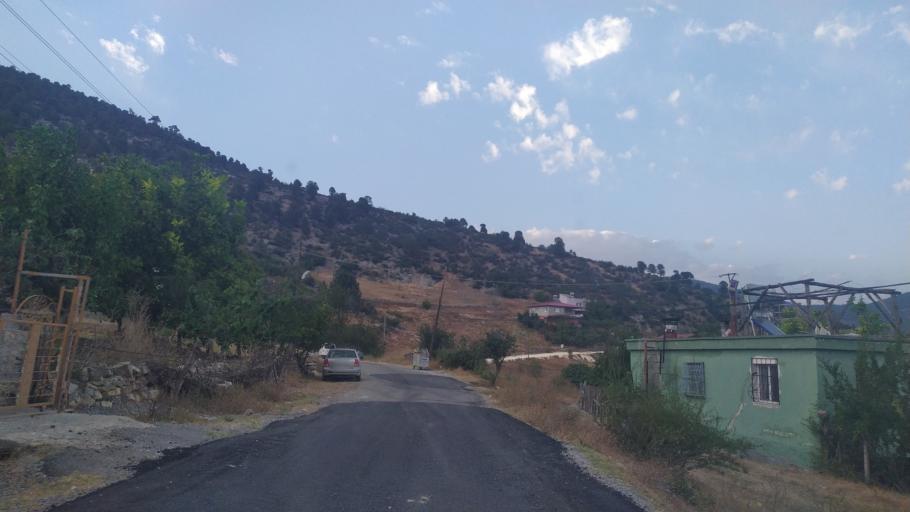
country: TR
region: Mersin
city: Camliyayla
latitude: 37.2294
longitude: 34.7102
